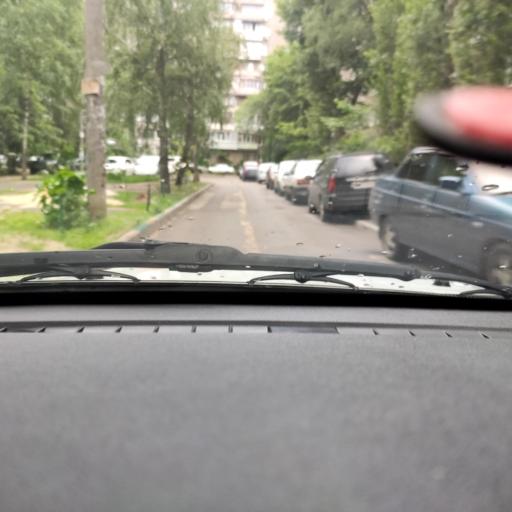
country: RU
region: Voronezj
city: Pridonskoy
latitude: 51.6501
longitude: 39.1200
